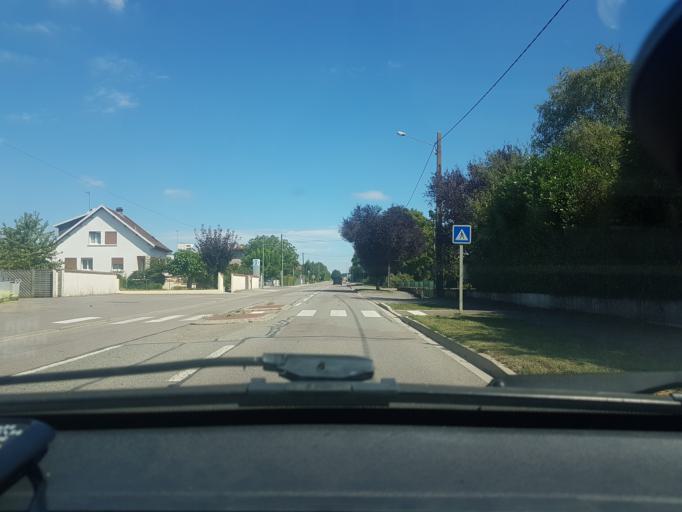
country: FR
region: Bourgogne
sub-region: Departement de la Cote-d'Or
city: Mirebeau-sur-Beze
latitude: 47.4000
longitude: 5.3228
